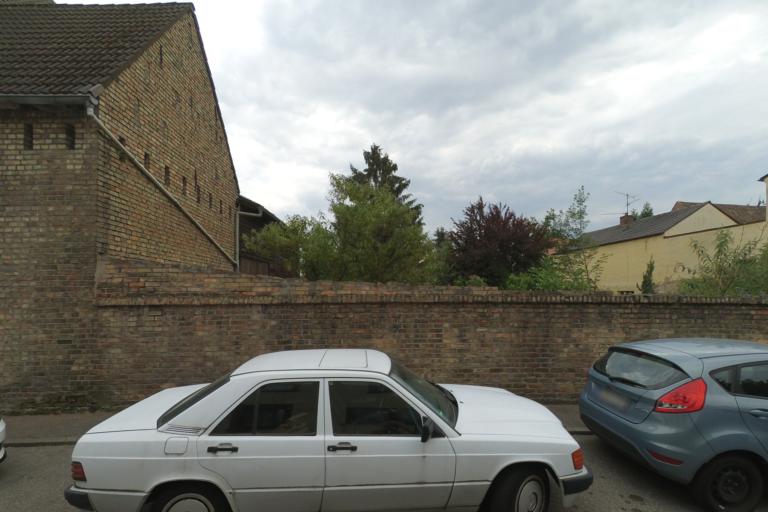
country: DE
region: Hesse
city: Viernheim
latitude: 49.5354
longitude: 8.5754
